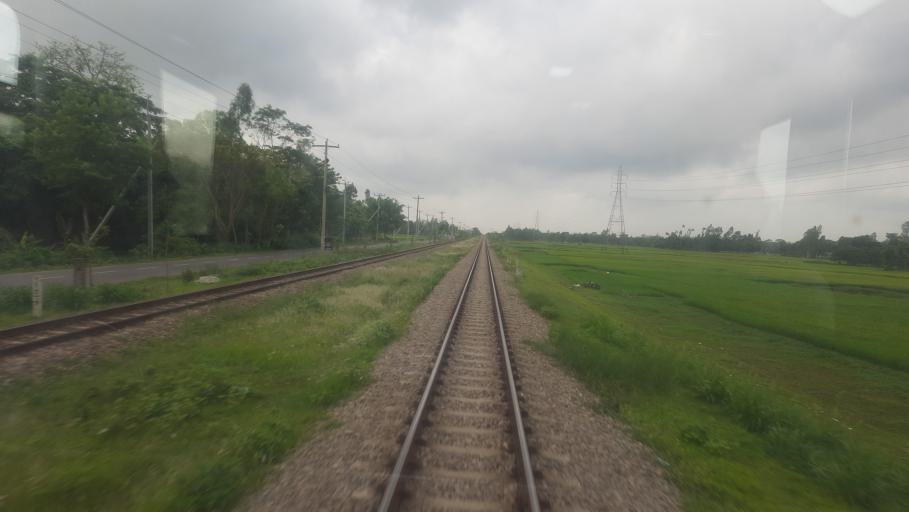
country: BD
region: Dhaka
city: Bhairab Bazar
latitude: 23.9875
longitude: 90.8553
